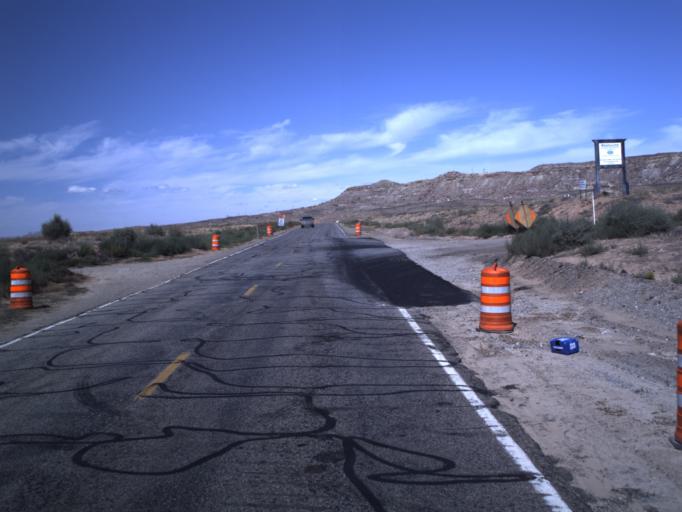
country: US
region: Utah
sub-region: San Juan County
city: Blanding
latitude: 37.2280
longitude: -109.2120
